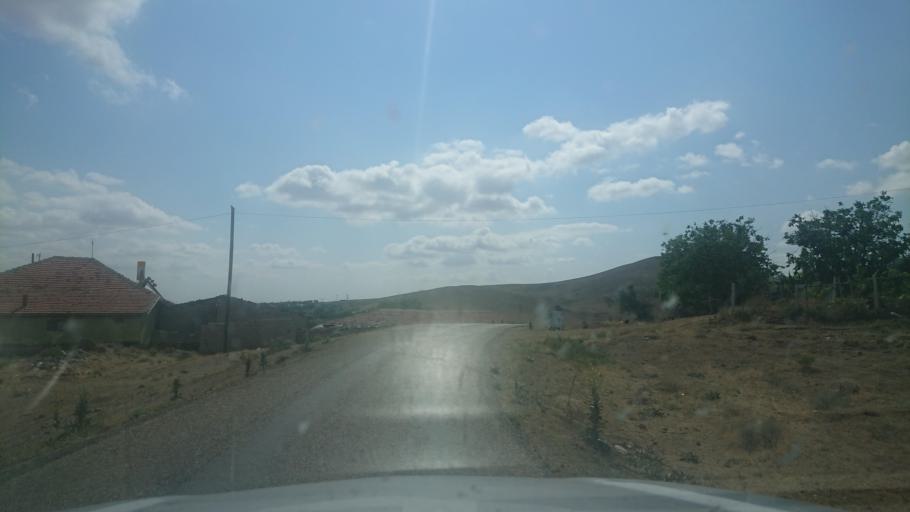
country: TR
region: Aksaray
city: Sariyahsi
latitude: 39.0115
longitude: 33.9457
